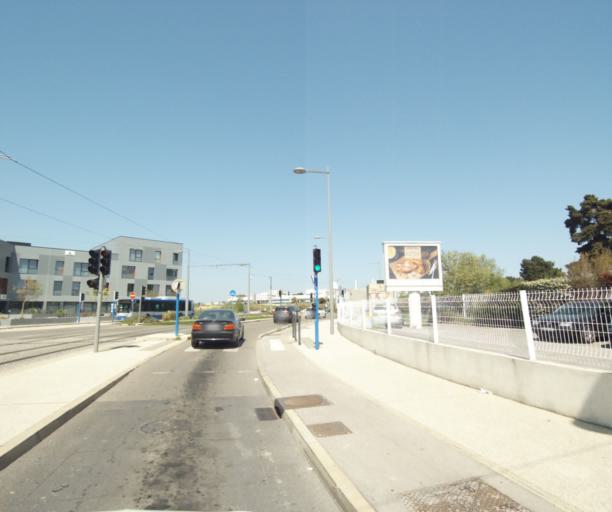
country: FR
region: Languedoc-Roussillon
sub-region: Departement de l'Herault
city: Juvignac
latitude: 43.6166
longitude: 3.8260
